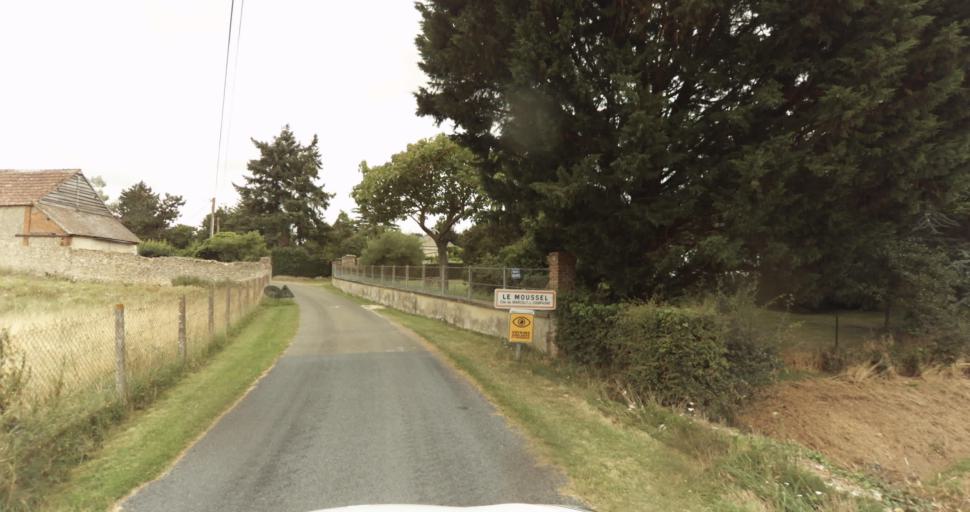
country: FR
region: Haute-Normandie
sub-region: Departement de l'Eure
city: La Madeleine-de-Nonancourt
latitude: 48.8205
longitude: 1.1797
